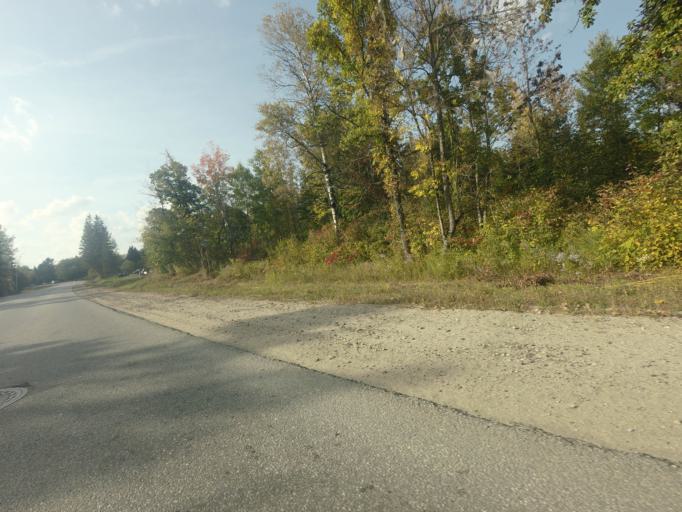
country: CA
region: Quebec
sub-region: Outaouais
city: Maniwaki
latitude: 46.3652
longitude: -75.9941
